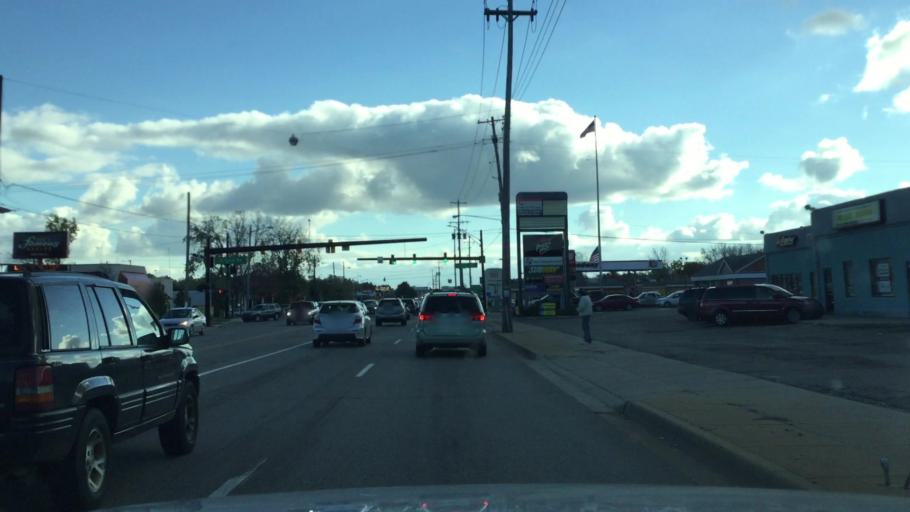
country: US
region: Michigan
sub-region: Kalamazoo County
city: Portage
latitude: 42.2459
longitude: -85.5897
